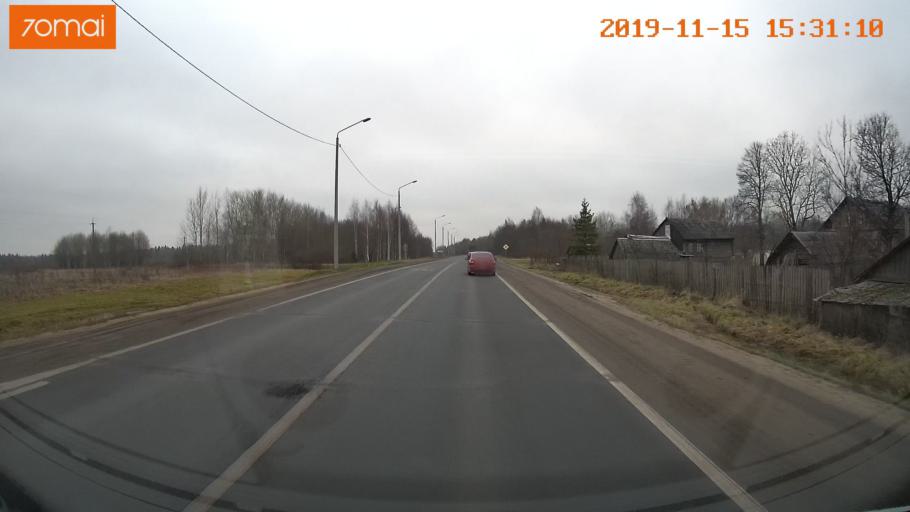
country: RU
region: Jaroslavl
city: Danilov
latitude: 58.1028
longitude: 40.1092
